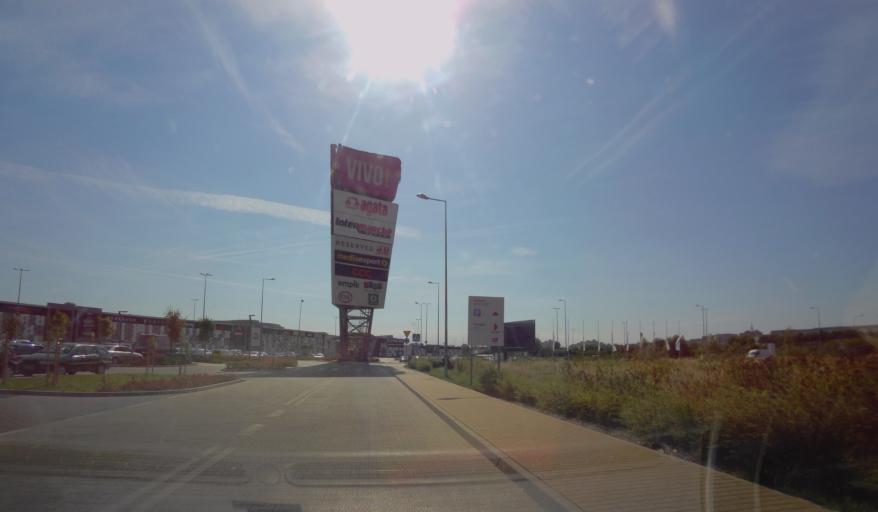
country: PL
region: Subcarpathian Voivodeship
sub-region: Powiat stalowowolski
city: Stalowa Wola
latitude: 50.5866
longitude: 22.0620
